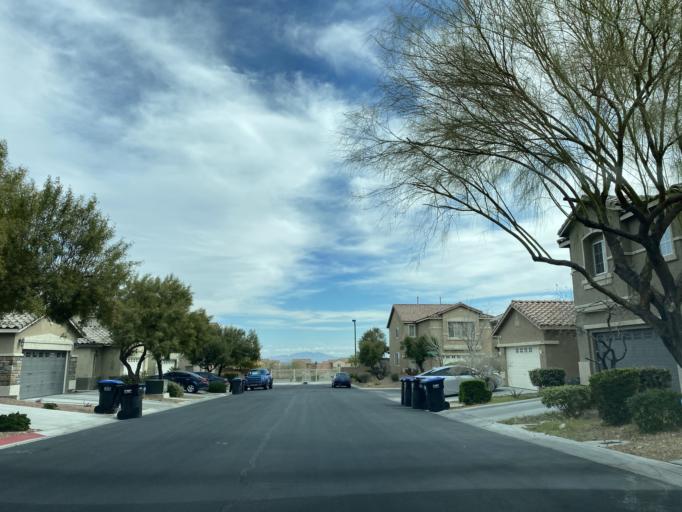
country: US
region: Nevada
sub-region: Clark County
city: Summerlin South
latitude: 36.3045
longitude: -115.3023
